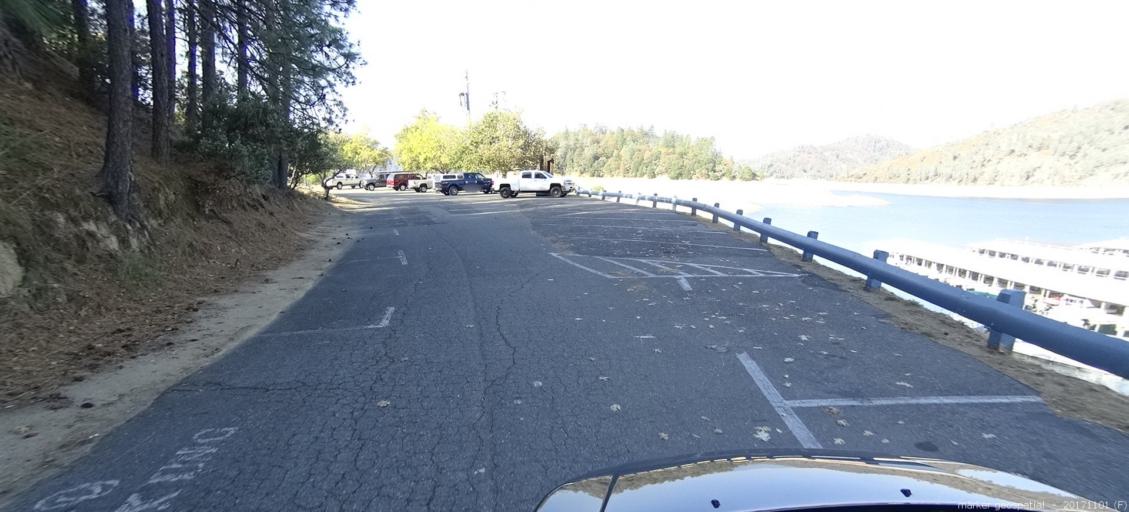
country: US
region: California
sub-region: Shasta County
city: Shasta Lake
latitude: 40.7568
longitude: -122.3236
